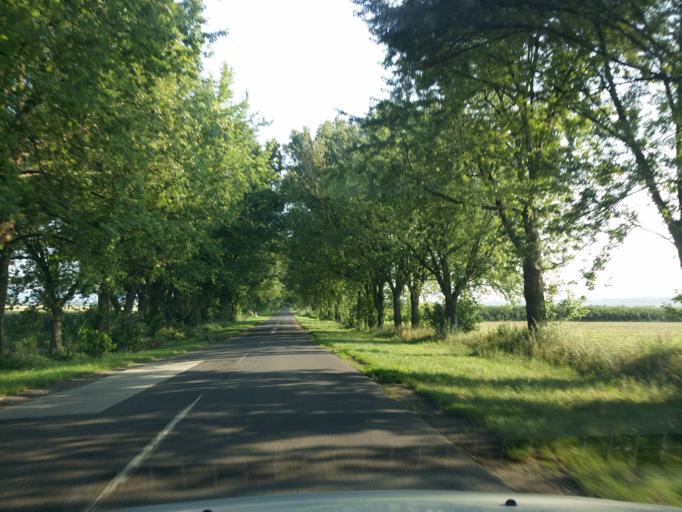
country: HU
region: Borsod-Abauj-Zemplen
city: Gonc
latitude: 48.4332
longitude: 21.2384
